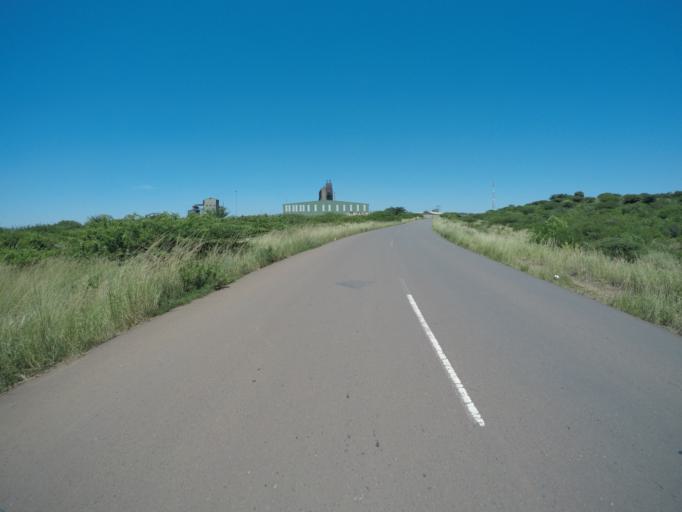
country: ZA
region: KwaZulu-Natal
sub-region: uThungulu District Municipality
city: Empangeni
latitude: -28.7178
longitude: 31.8684
